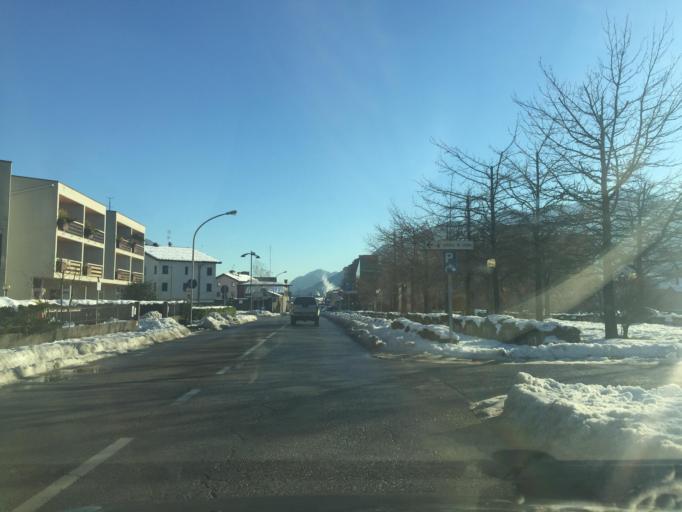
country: IT
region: Friuli Venezia Giulia
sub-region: Provincia di Udine
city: Tolmezzo
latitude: 46.4074
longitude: 13.0094
